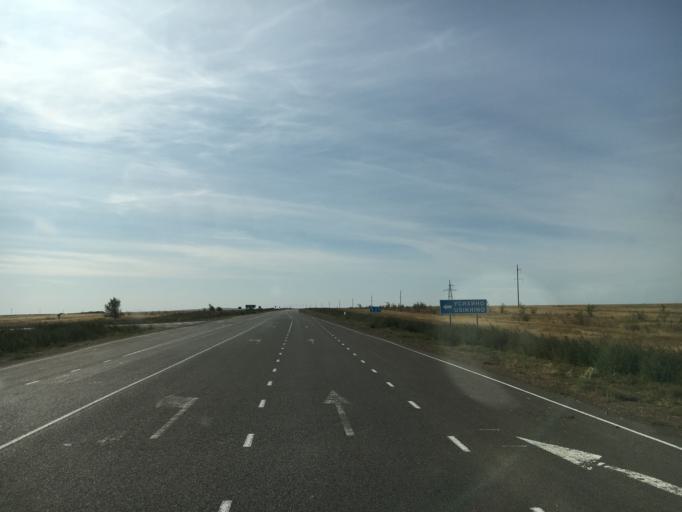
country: KZ
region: Batys Qazaqstan
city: Peremetnoe
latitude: 51.1203
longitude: 50.7396
